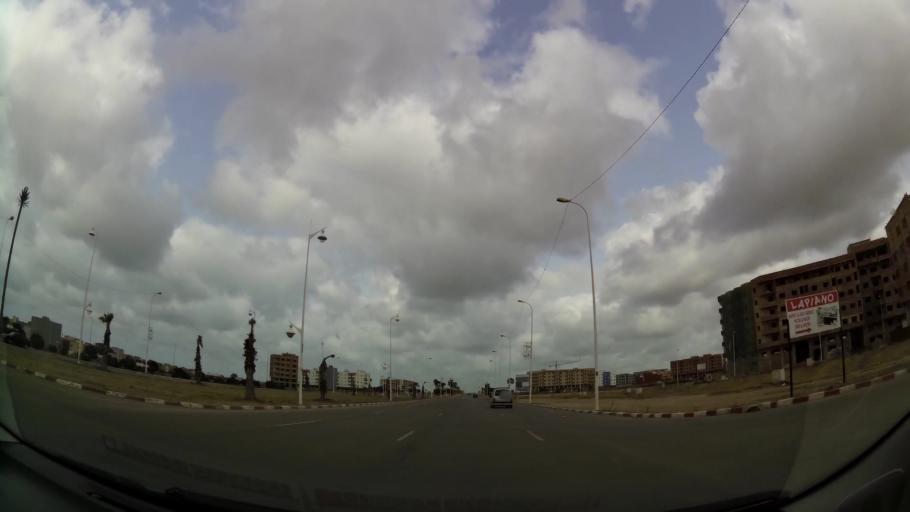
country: MA
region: Oriental
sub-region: Nador
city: Nador
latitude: 35.1531
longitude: -2.9154
